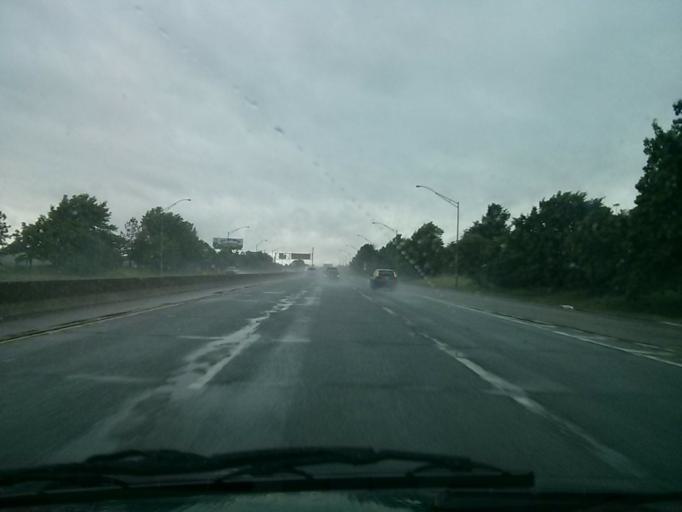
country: US
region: Oklahoma
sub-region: Tulsa County
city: Tulsa
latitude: 36.1250
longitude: -96.0087
